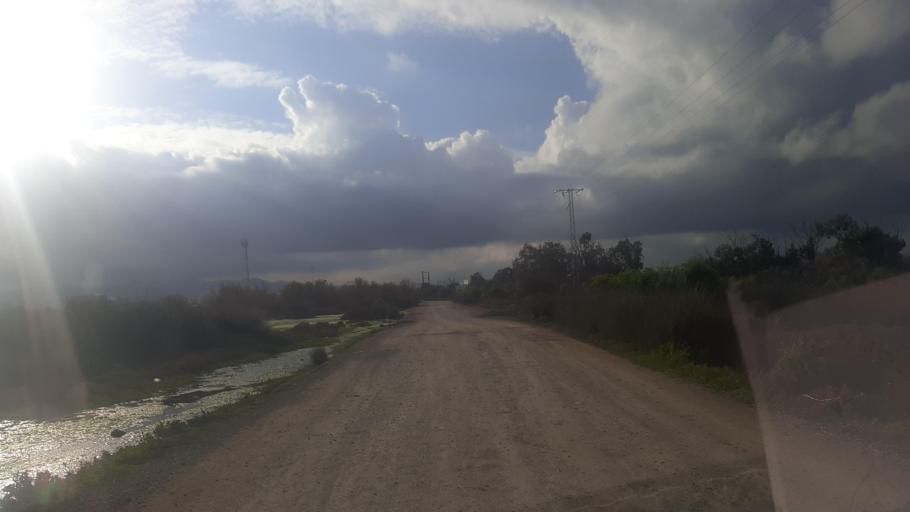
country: TN
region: Nabul
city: Manzil Bu Zalafah
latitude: 36.7135
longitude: 10.4882
